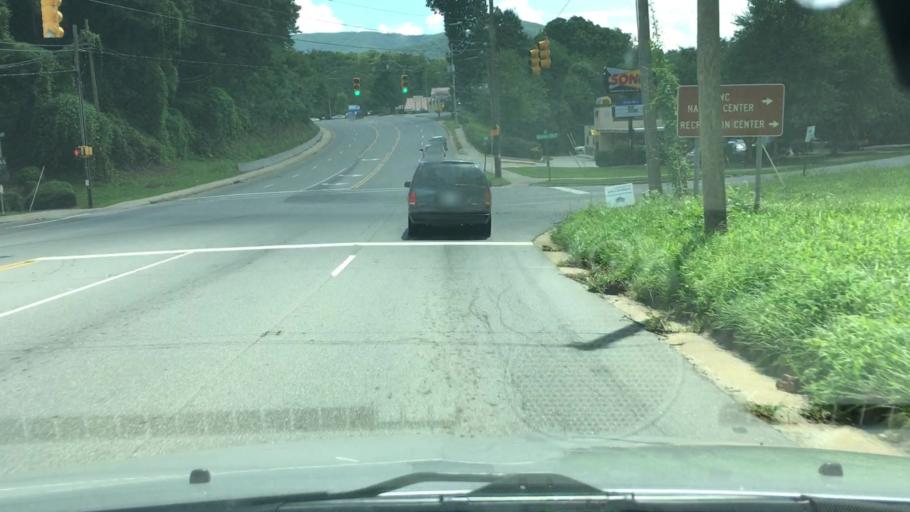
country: US
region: North Carolina
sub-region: Buncombe County
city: Asheville
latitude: 35.5889
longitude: -82.4956
